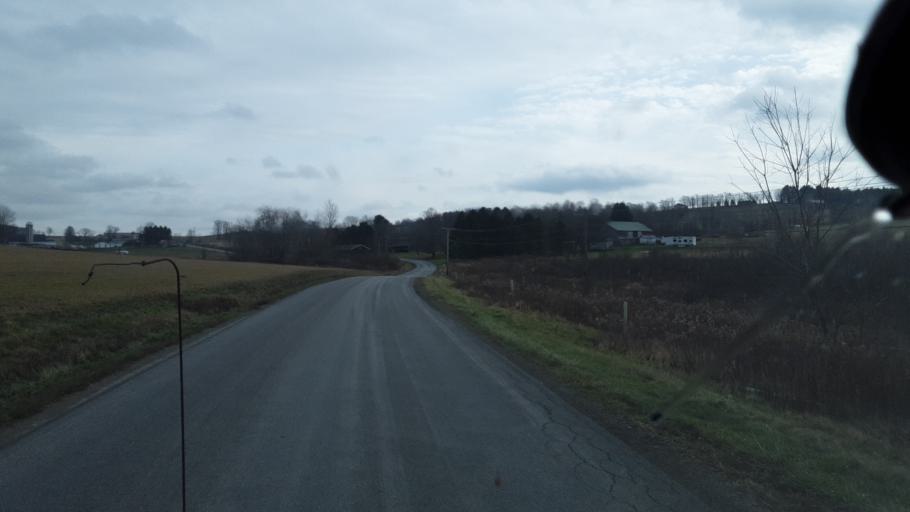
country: US
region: Pennsylvania
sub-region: Potter County
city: Galeton
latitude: 41.8876
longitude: -77.7705
